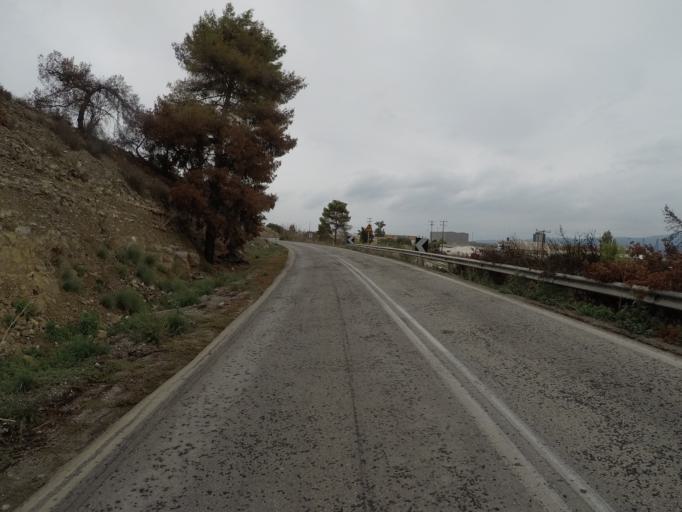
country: GR
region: Peloponnese
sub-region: Nomos Korinthias
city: Isthmia
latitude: 37.9210
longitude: 23.0556
